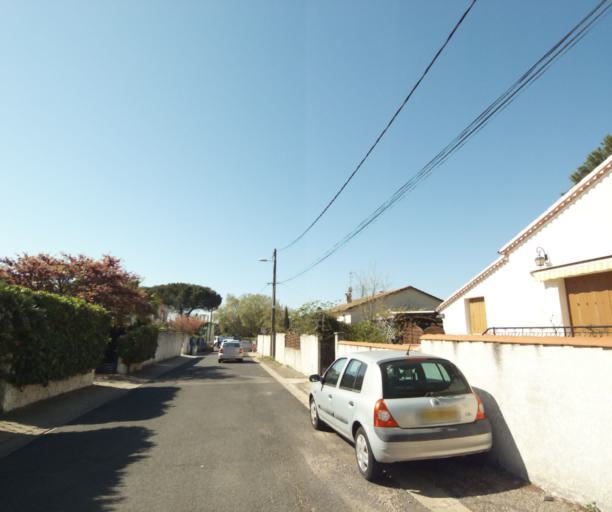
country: FR
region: Languedoc-Roussillon
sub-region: Departement de l'Herault
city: Le Cres
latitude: 43.6440
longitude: 3.9363
